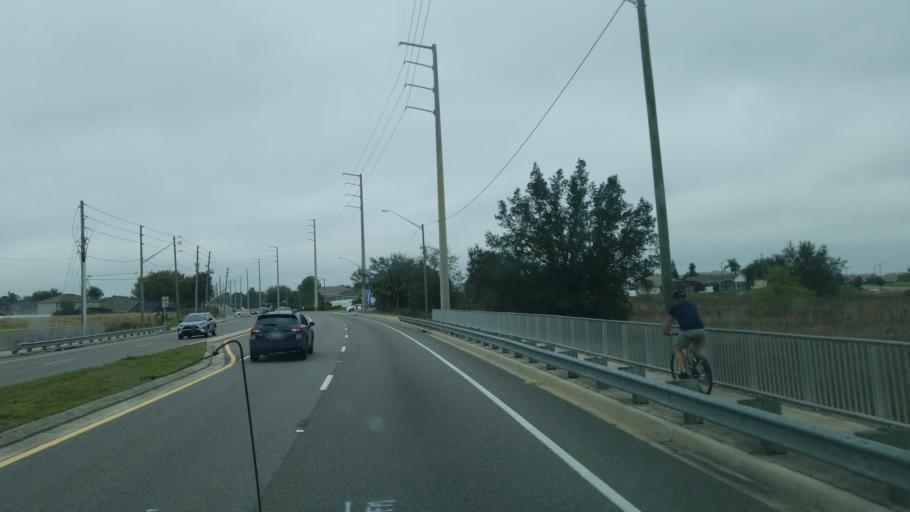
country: US
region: Florida
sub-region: Polk County
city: Loughman
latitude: 28.2577
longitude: -81.6379
